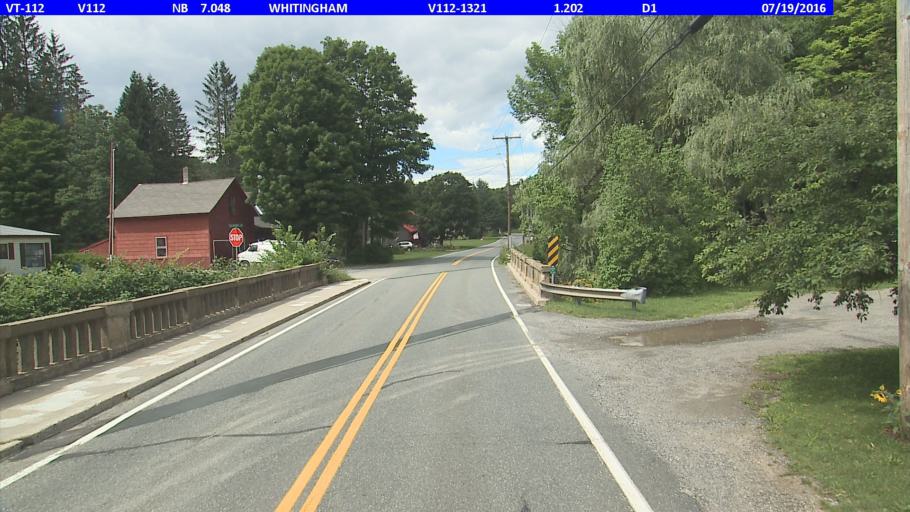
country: US
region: Vermont
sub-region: Windham County
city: Dover
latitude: 42.7914
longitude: -72.8201
